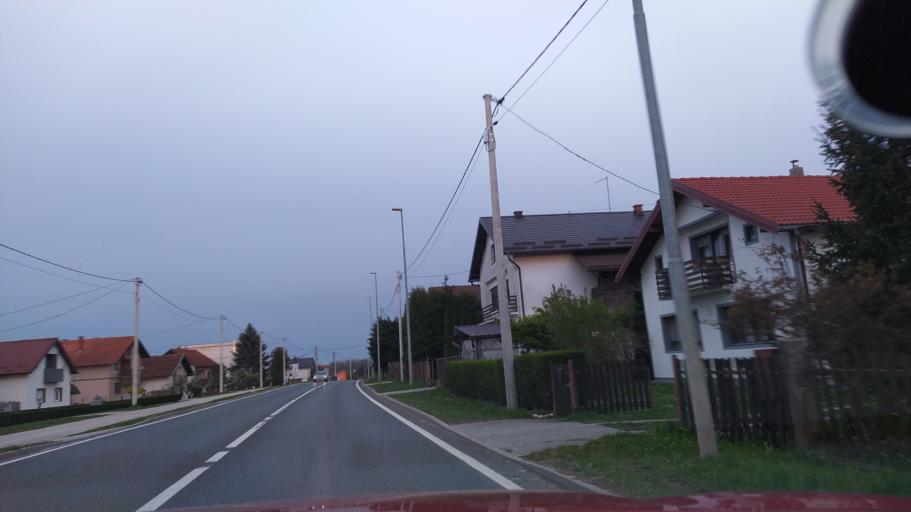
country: HR
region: Koprivnicko-Krizevacka
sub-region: Grad Koprivnica
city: Koprivnica
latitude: 46.1827
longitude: 16.7784
